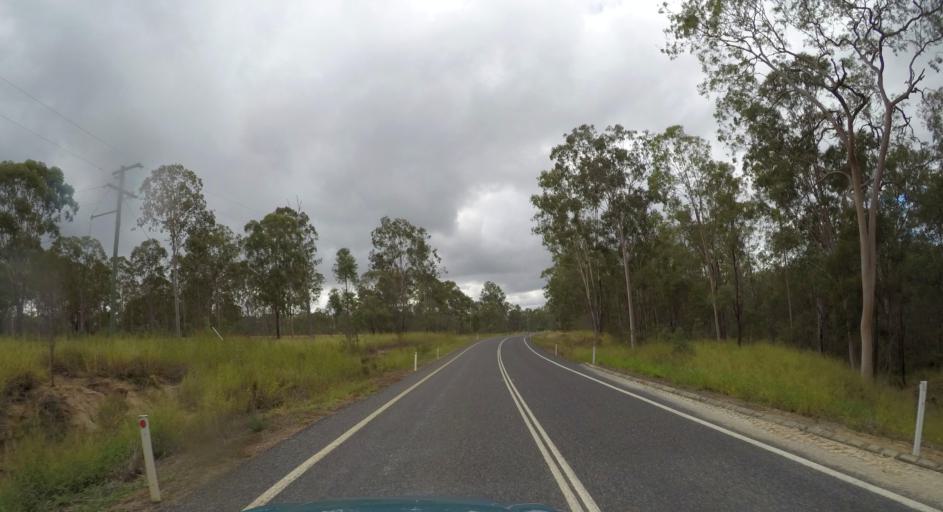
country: AU
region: Queensland
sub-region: North Burnett
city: Gayndah
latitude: -25.3586
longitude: 151.1185
